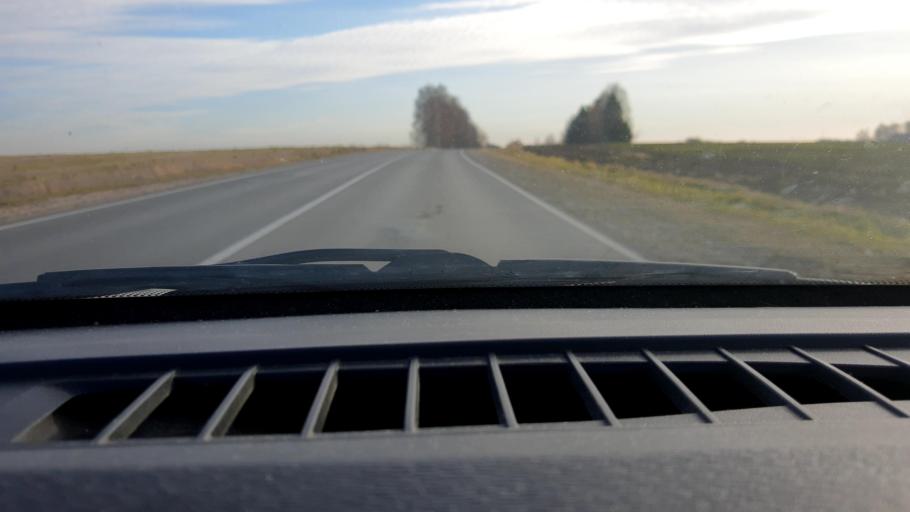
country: RU
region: Nizjnij Novgorod
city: Gorodets
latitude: 56.6281
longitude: 43.5428
